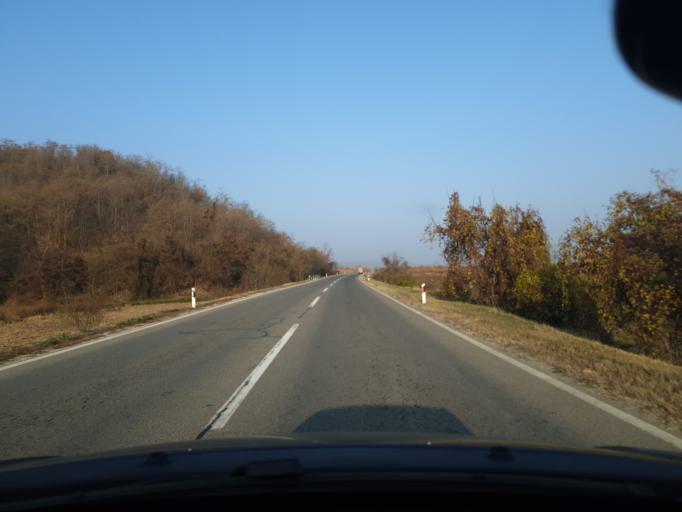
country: RS
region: Central Serbia
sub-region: Jablanicki Okrug
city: Leskovac
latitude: 42.9185
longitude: 22.0266
